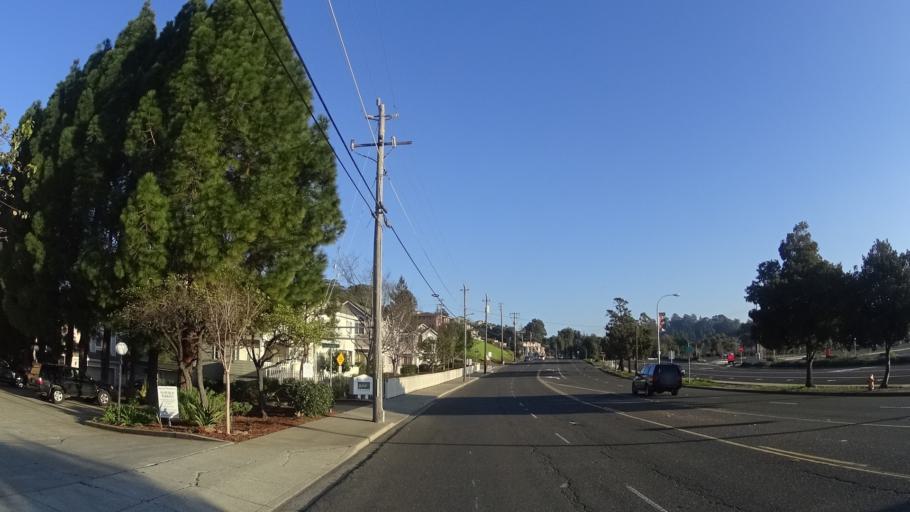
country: US
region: California
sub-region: Alameda County
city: Fairview
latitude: 37.6597
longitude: -122.0528
